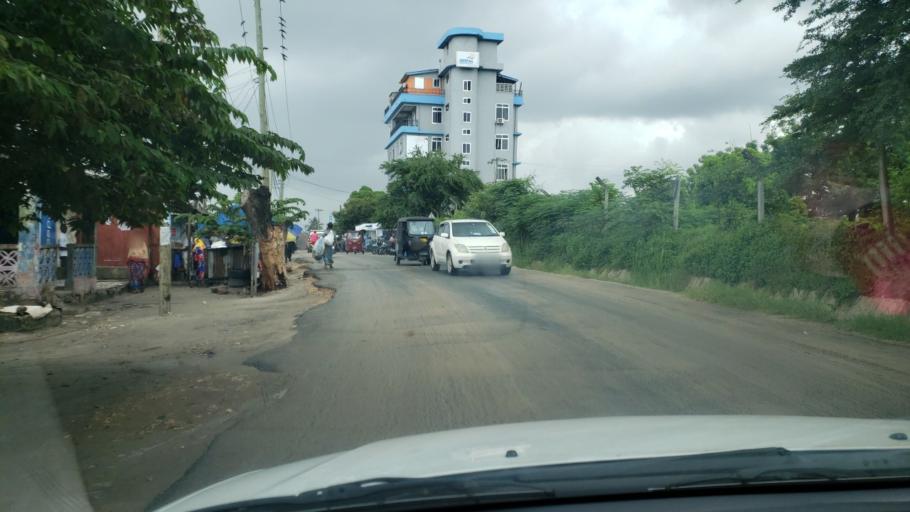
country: TZ
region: Dar es Salaam
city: Magomeni
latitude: -6.8068
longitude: 39.2501
